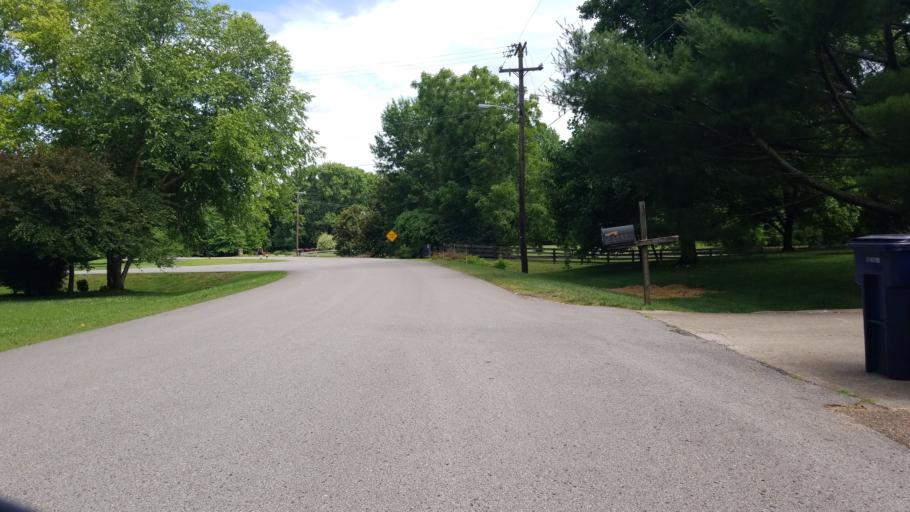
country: US
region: Tennessee
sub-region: Davidson County
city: Forest Hills
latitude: 36.0384
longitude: -86.8428
